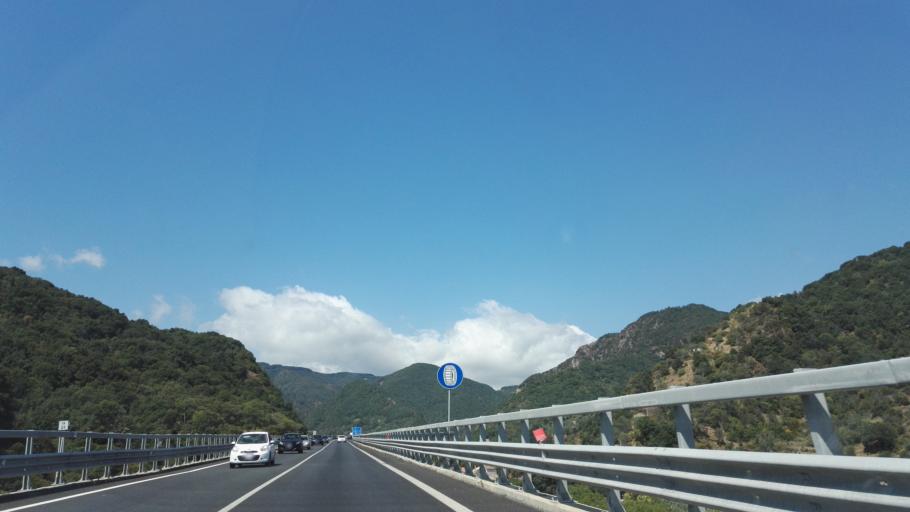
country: IT
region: Calabria
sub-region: Provincia di Reggio Calabria
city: Mammola
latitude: 38.3589
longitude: 16.2194
